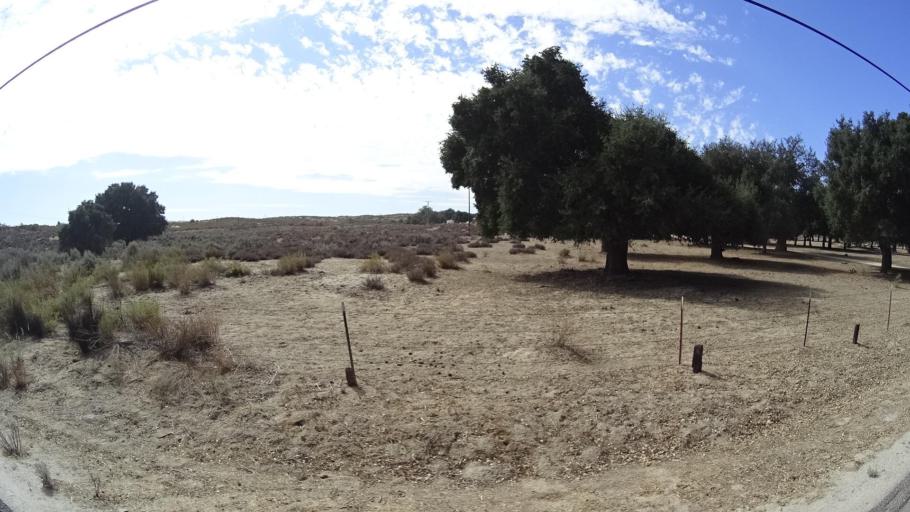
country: US
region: California
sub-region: San Diego County
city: Campo
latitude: 32.6894
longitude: -116.2936
